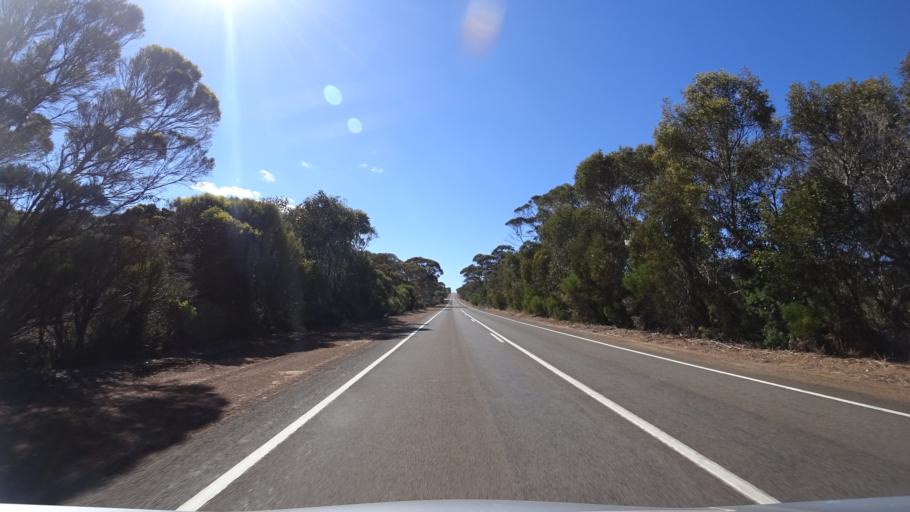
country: AU
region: South Australia
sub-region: Kangaroo Island
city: Kingscote
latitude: -35.7492
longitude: 137.5928
